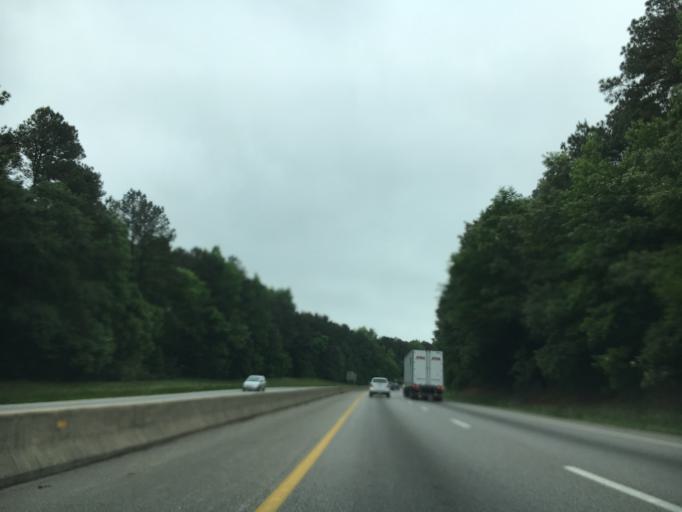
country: US
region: Virginia
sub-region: City of Petersburg
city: Petersburg
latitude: 37.2025
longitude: -77.4144
